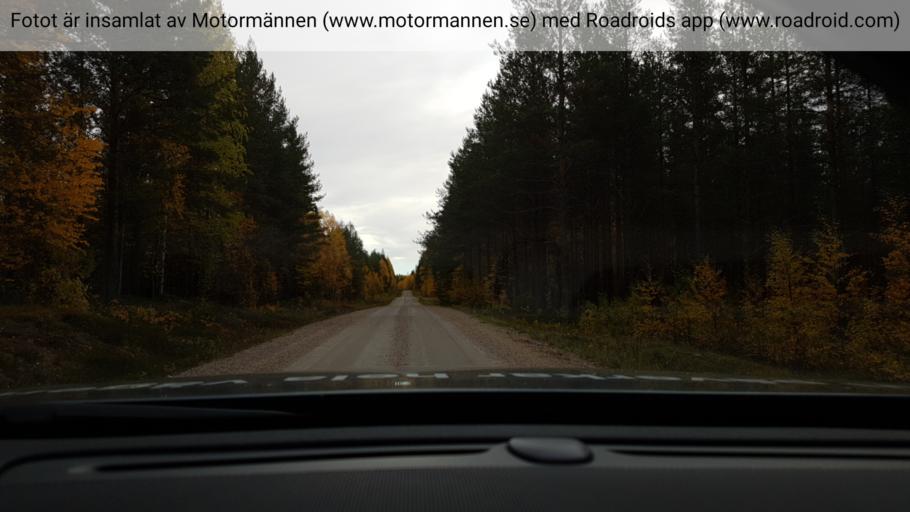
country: SE
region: Norrbotten
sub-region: Overkalix Kommun
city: OEverkalix
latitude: 66.2786
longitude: 22.9812
